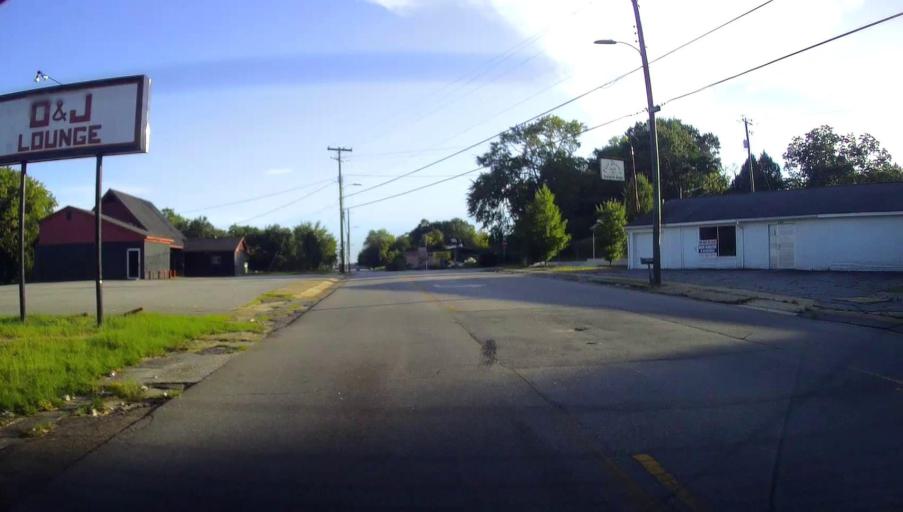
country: US
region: Alabama
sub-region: Russell County
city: Phenix City
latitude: 32.4490
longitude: -85.0082
